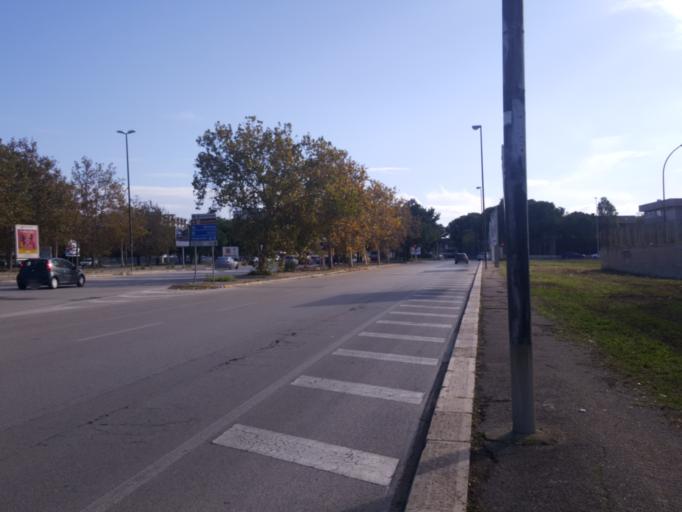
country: IT
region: Apulia
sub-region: Provincia di Bari
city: Triggiano
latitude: 41.1031
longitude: 16.9072
